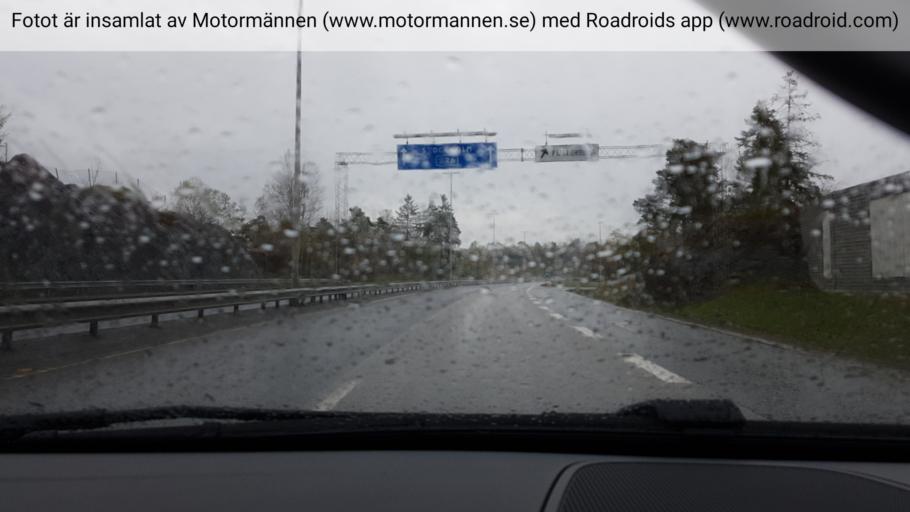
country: SE
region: Stockholm
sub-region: Huddinge Kommun
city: Huddinge
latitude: 59.2388
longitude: 17.9769
